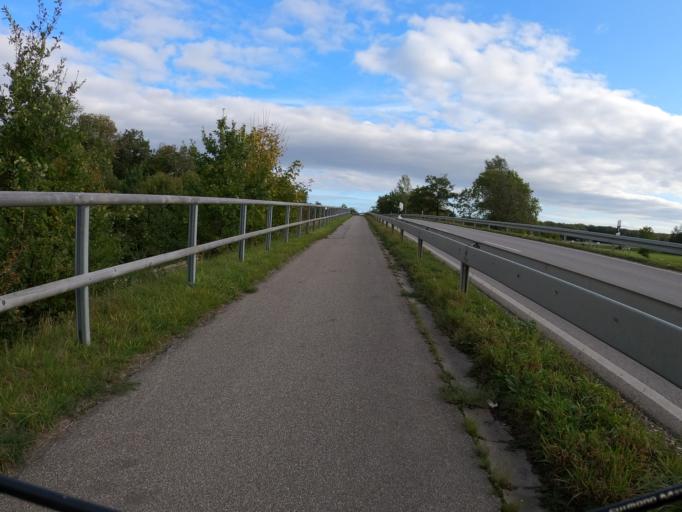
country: DE
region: Bavaria
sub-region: Swabia
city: Holzheim
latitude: 48.4030
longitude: 10.0894
